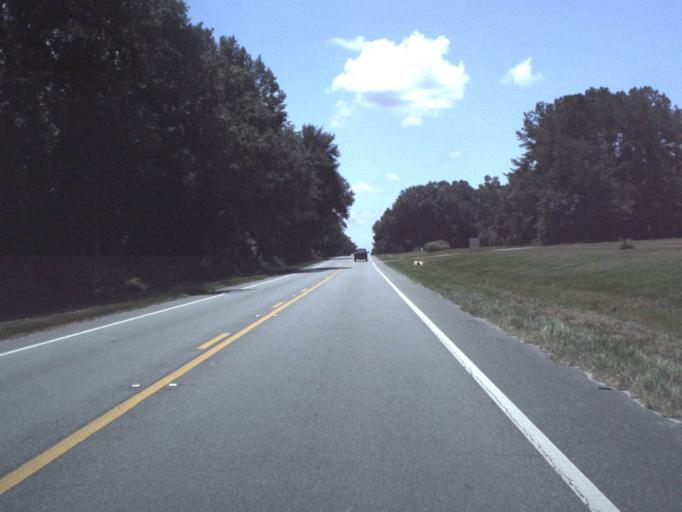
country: US
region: Florida
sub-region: Columbia County
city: Five Points
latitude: 30.2957
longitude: -82.7070
